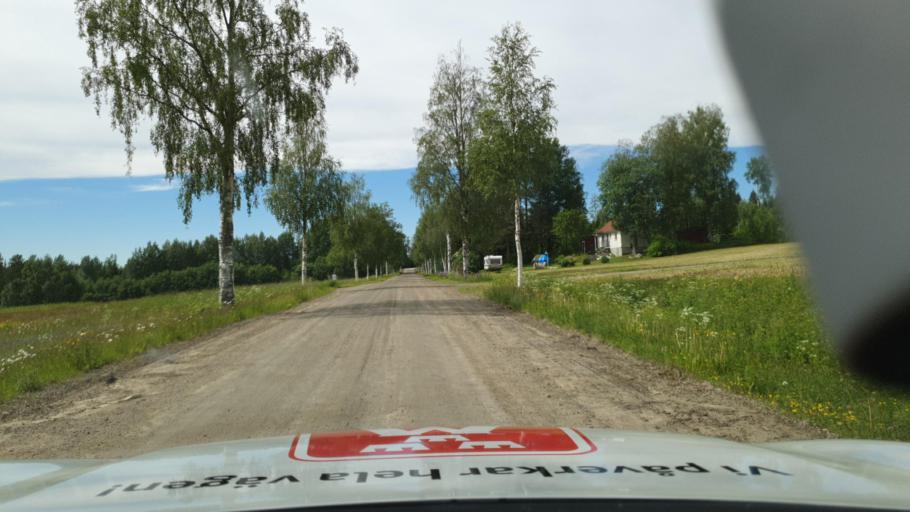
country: SE
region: Vaesterbotten
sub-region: Skelleftea Kommun
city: Burtraesk
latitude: 64.4795
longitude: 20.4343
